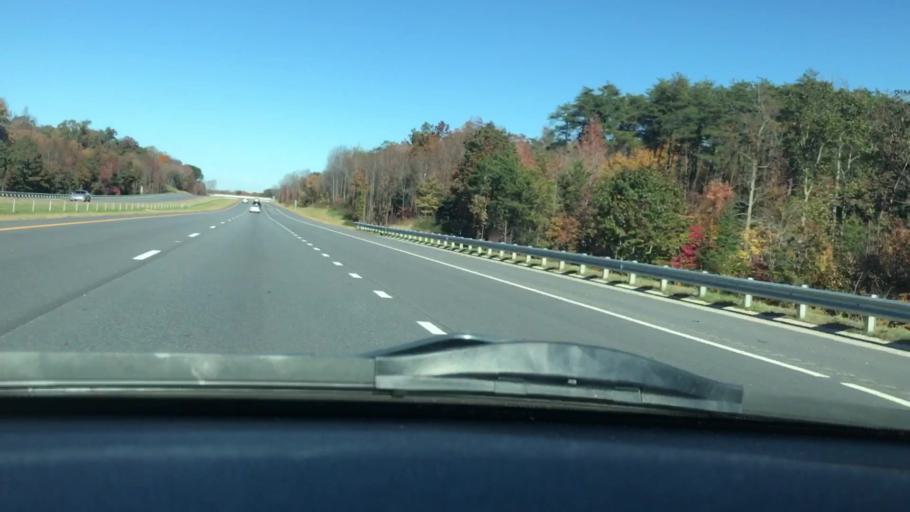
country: US
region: North Carolina
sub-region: Guilford County
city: Summerfield
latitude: 36.2070
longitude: -79.9232
